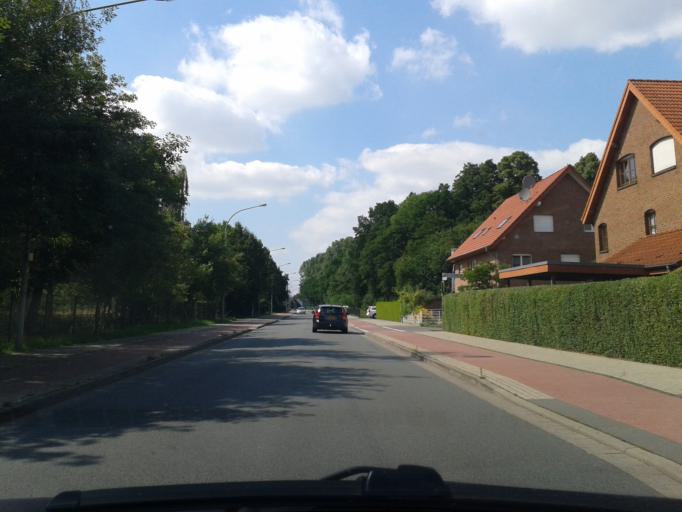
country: DE
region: North Rhine-Westphalia
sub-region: Regierungsbezirk Detmold
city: Paderborn
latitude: 51.7515
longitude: 8.7094
